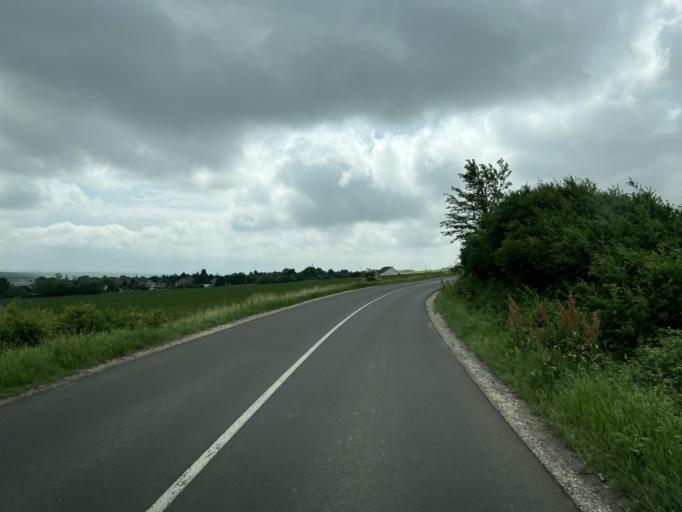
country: HU
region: Pest
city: Kartal
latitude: 47.7279
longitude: 19.5326
